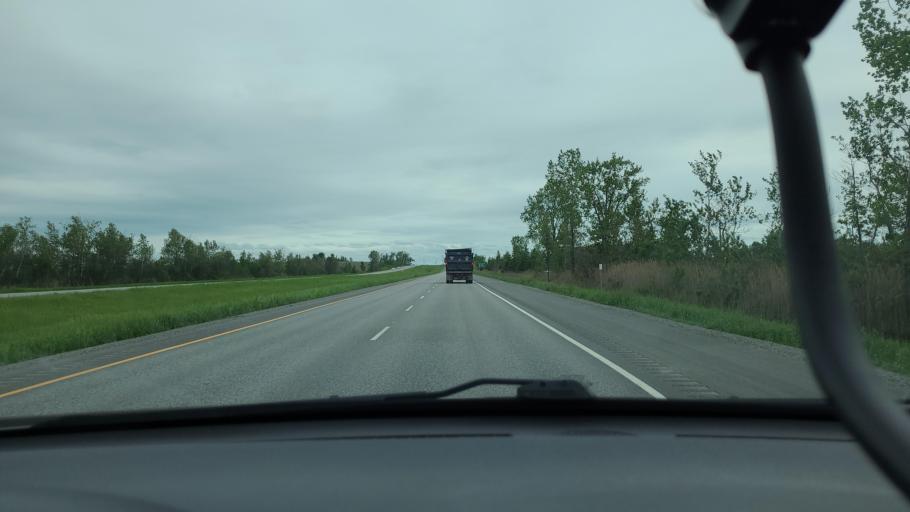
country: CA
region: Quebec
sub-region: Lanaudiere
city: Mascouche
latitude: 45.8312
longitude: -73.6139
